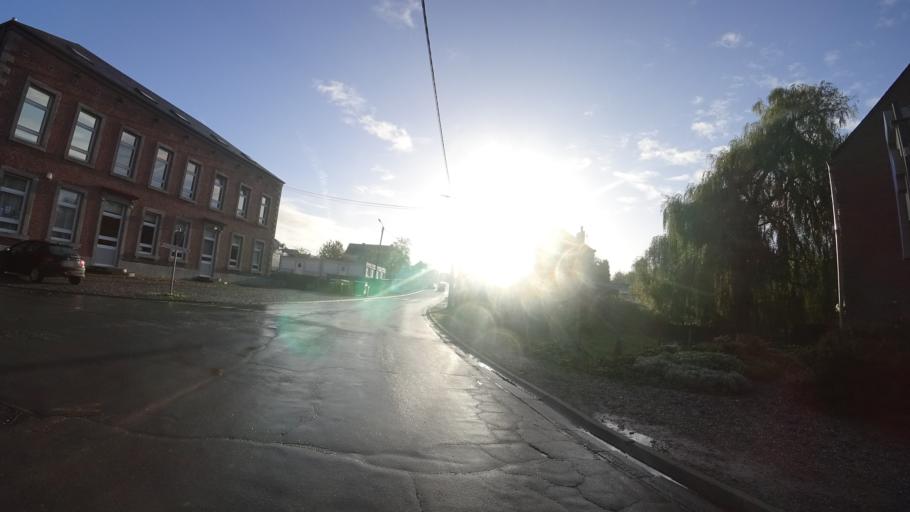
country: BE
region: Wallonia
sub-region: Province de Namur
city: Namur
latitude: 50.5057
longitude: 4.8015
